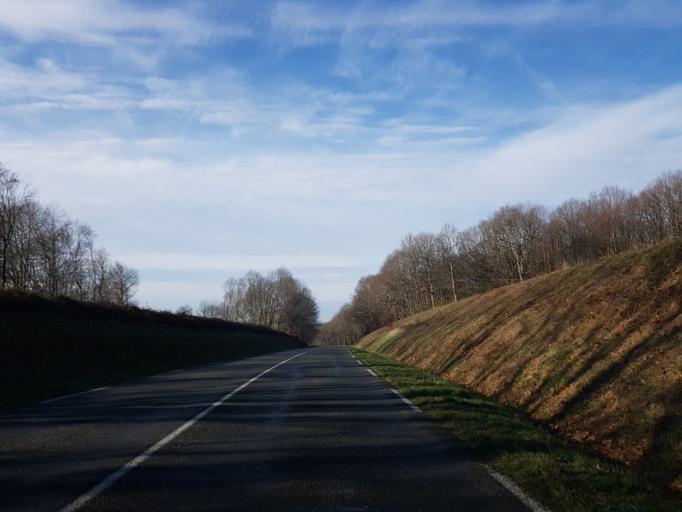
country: FR
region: Bourgogne
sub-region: Departement de Saone-et-Loire
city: Bourbon-Lancy
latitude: 46.6088
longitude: 3.8807
